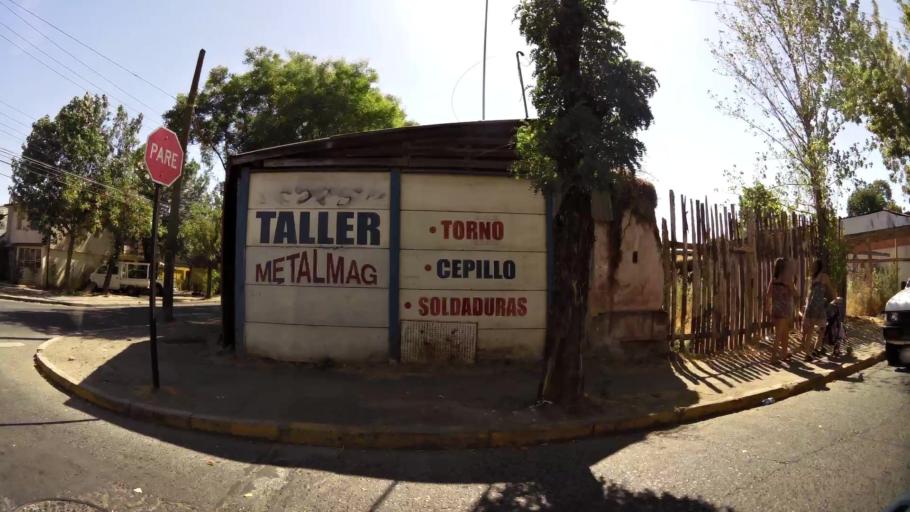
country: CL
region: Maule
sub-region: Provincia de Talca
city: Talca
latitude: -35.4334
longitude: -71.6603
